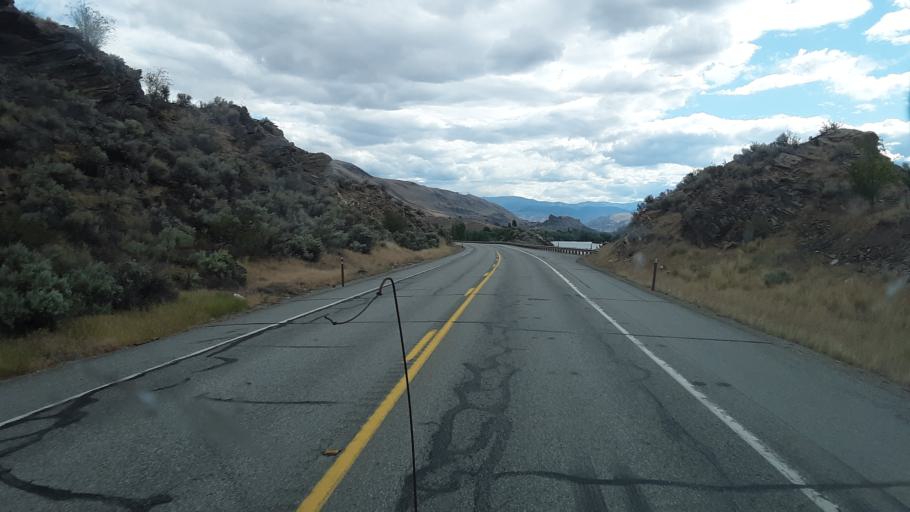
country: US
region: Washington
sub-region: Chelan County
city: Entiat
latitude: 47.5884
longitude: -120.2328
